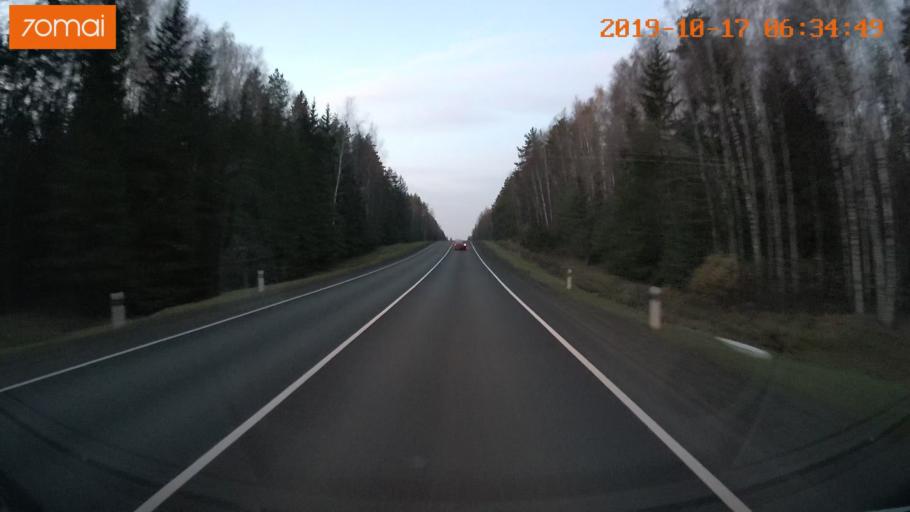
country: RU
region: Ivanovo
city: Novoye Leushino
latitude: 56.6991
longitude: 40.6321
